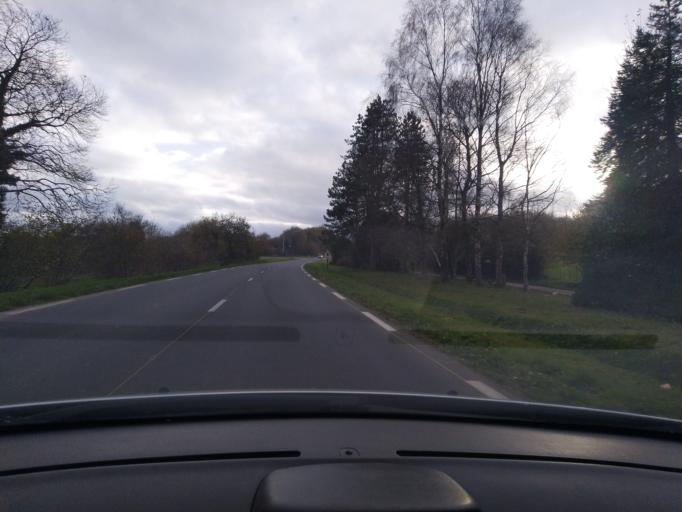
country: FR
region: Brittany
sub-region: Departement des Cotes-d'Armor
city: Plounevez-Moedec
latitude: 48.5682
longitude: -3.4954
